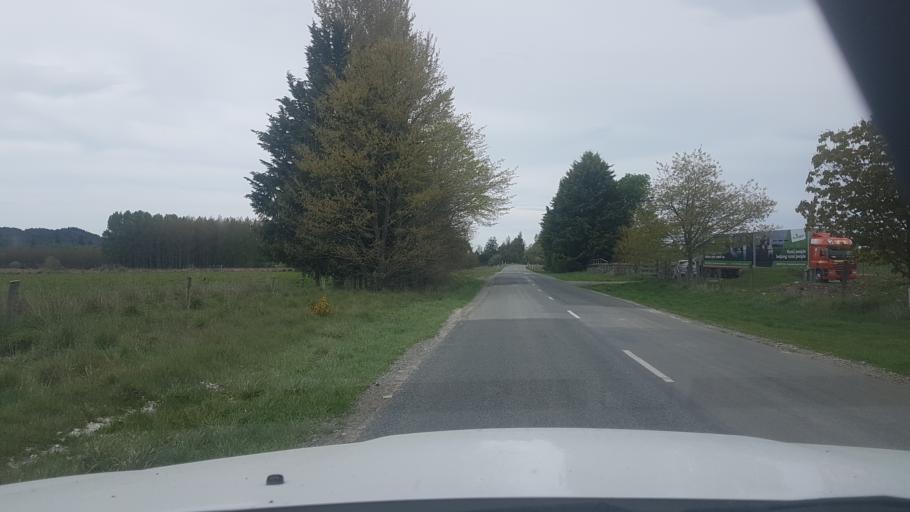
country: NZ
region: Canterbury
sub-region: Timaru District
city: Pleasant Point
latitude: -44.0787
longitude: 171.1764
